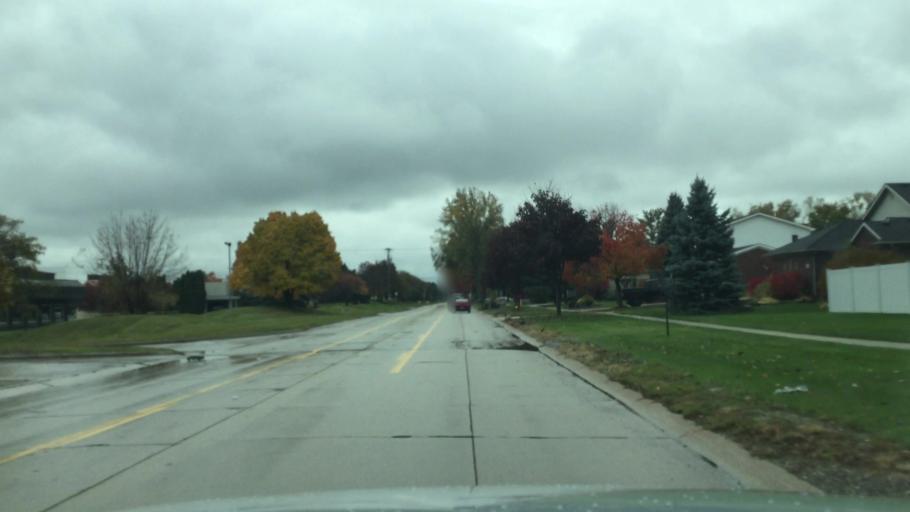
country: US
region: Michigan
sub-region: Macomb County
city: Utica
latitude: 42.6235
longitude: -83.0471
